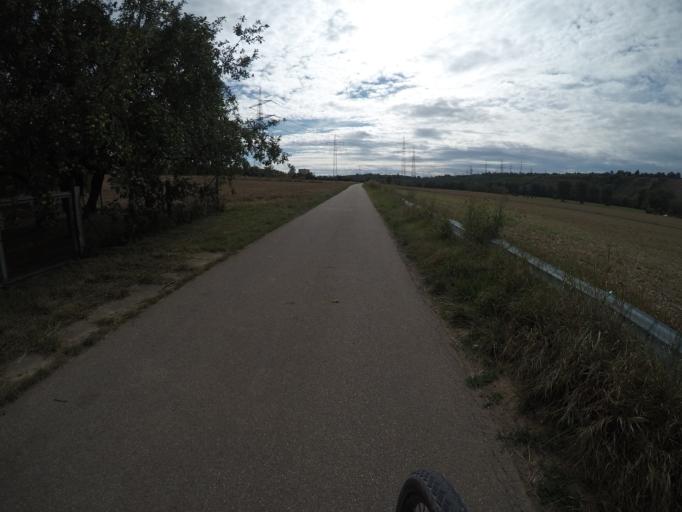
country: DE
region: Baden-Wuerttemberg
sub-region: Regierungsbezirk Stuttgart
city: Freiberg am Neckar
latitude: 48.9245
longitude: 9.2269
